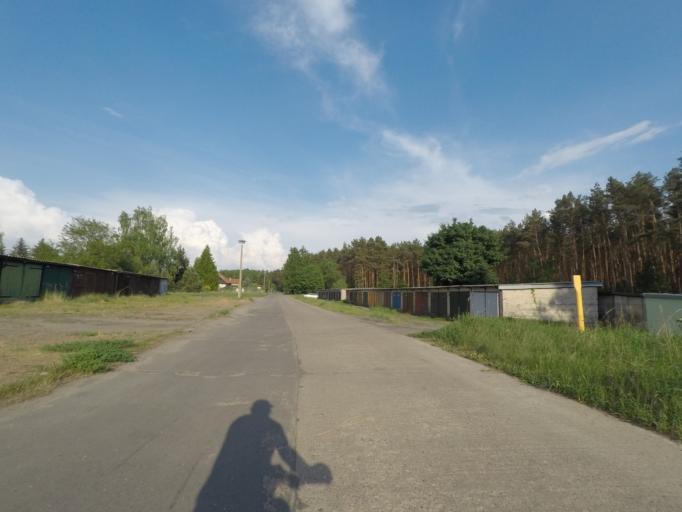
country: DE
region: Brandenburg
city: Melchow
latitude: 52.8312
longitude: 13.7323
